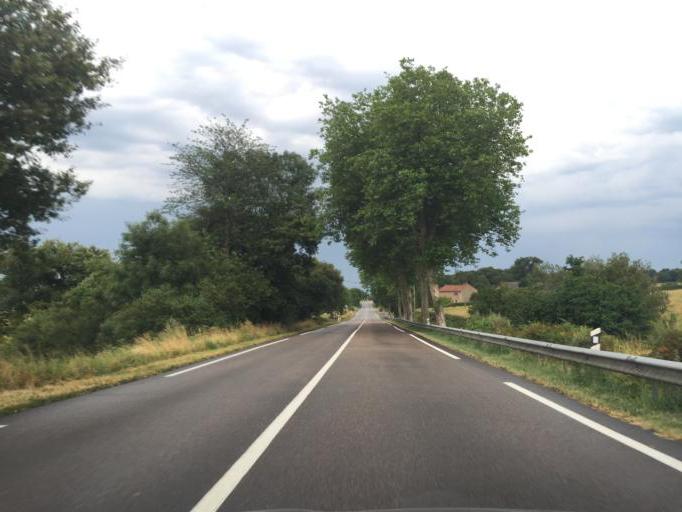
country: FR
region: Rhone-Alpes
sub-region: Departement de la Loire
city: La Pacaudiere
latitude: 46.2039
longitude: 3.8210
